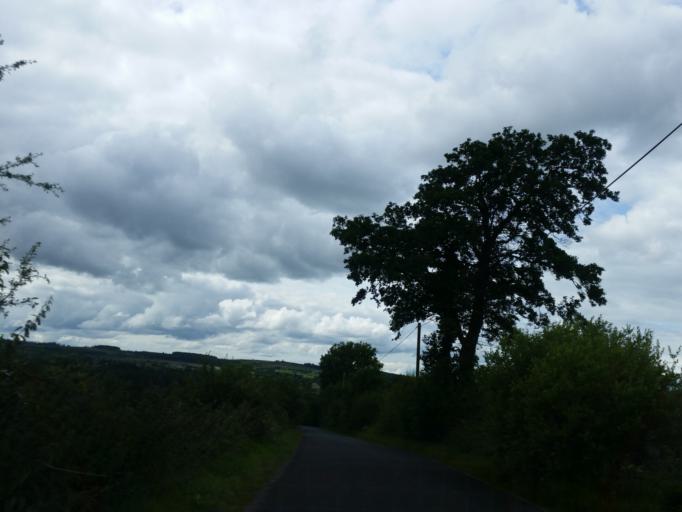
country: GB
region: Northern Ireland
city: Fivemiletown
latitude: 54.2879
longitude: -7.2778
